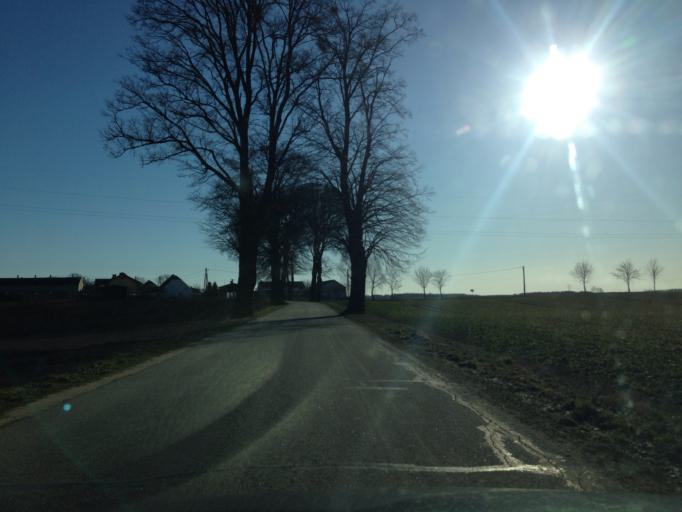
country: PL
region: Kujawsko-Pomorskie
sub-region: Powiat brodnicki
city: Brzozie
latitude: 53.2943
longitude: 19.6535
